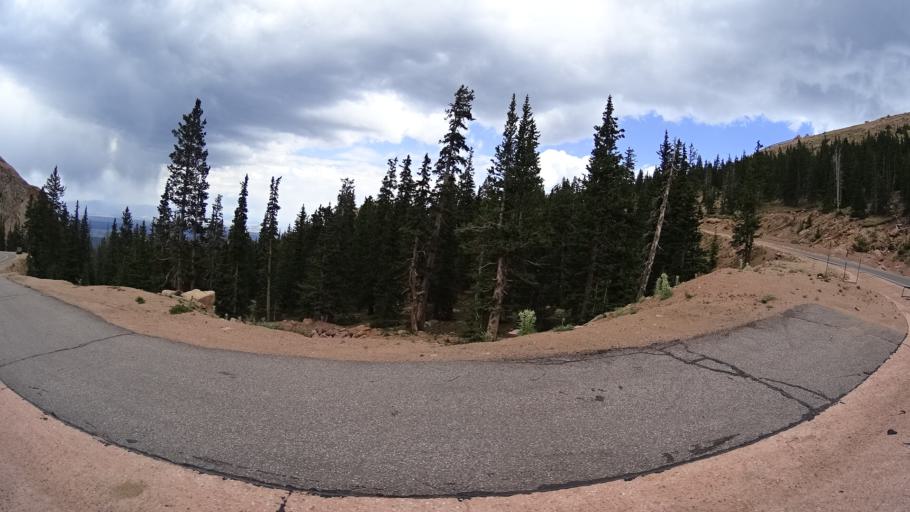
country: US
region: Colorado
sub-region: El Paso County
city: Cascade-Chipita Park
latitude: 38.8723
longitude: -105.0709
